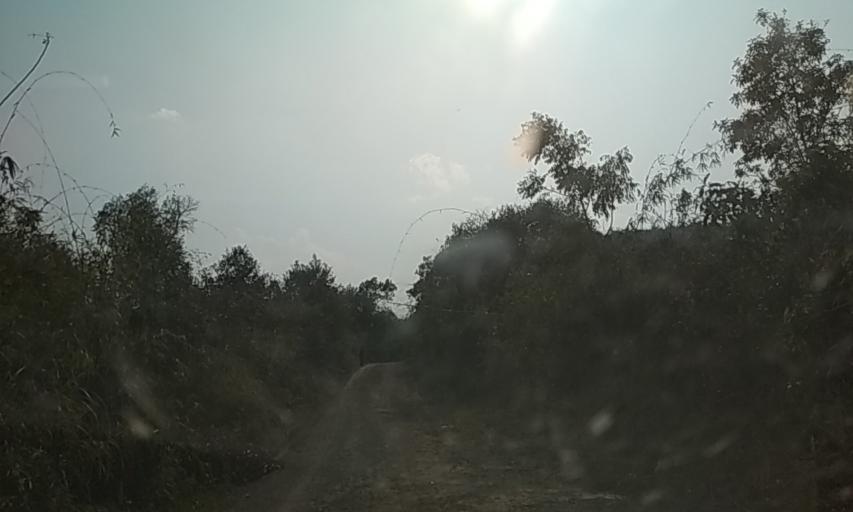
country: LA
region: Louangphabang
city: Louangphabang
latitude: 20.0369
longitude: 101.8261
